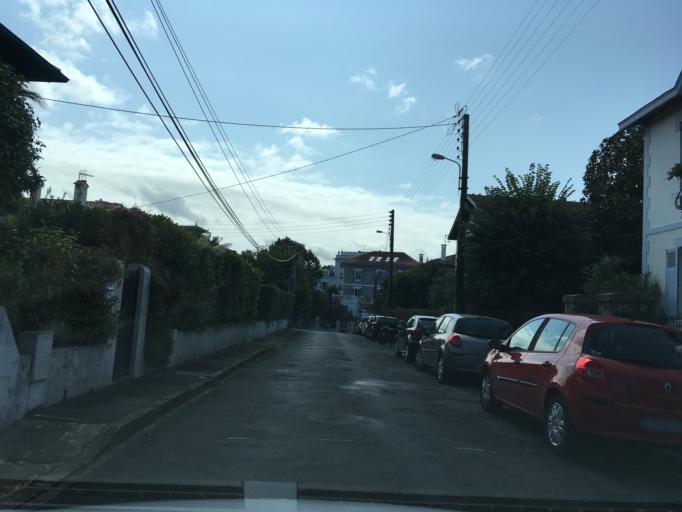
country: FR
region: Aquitaine
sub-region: Departement des Pyrenees-Atlantiques
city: Bayonne
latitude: 43.4953
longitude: -1.4898
